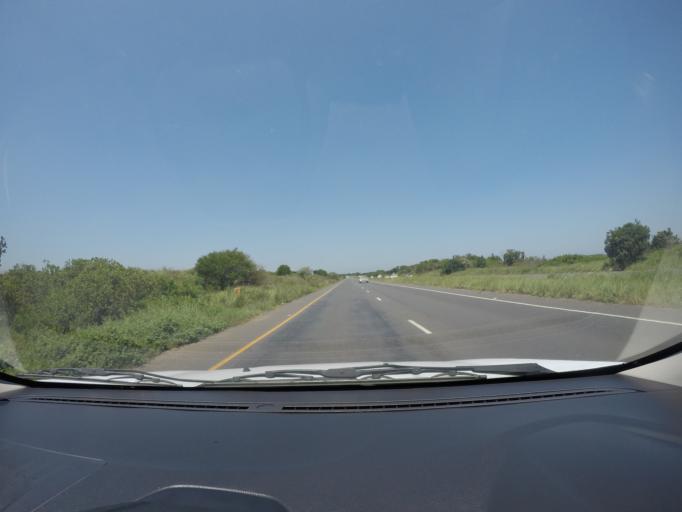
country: ZA
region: KwaZulu-Natal
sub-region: uThungulu District Municipality
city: Richards Bay
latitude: -28.7800
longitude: 31.9930
